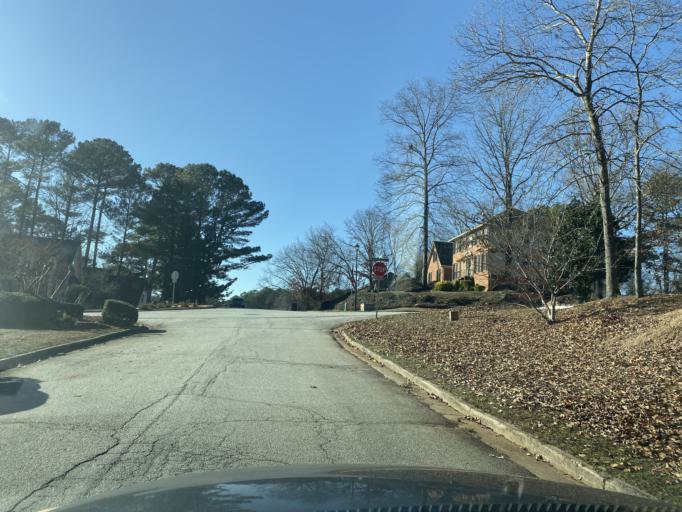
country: US
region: Georgia
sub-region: DeKalb County
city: Pine Mountain
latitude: 33.6820
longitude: -84.1589
